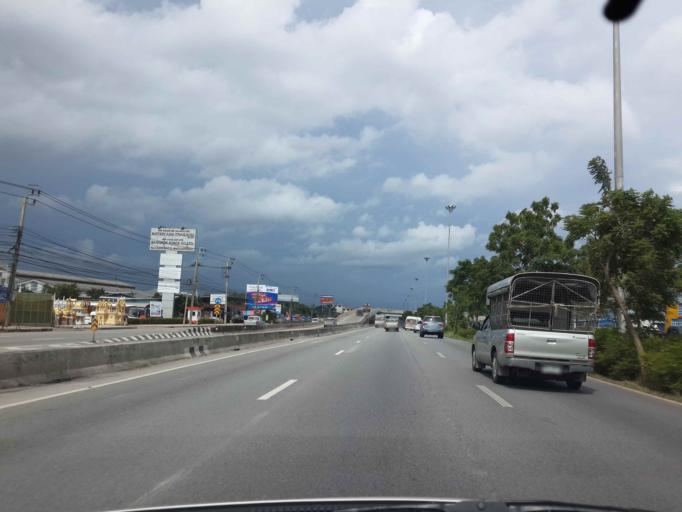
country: TH
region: Bangkok
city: Bang Bon
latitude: 13.6109
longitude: 100.3785
